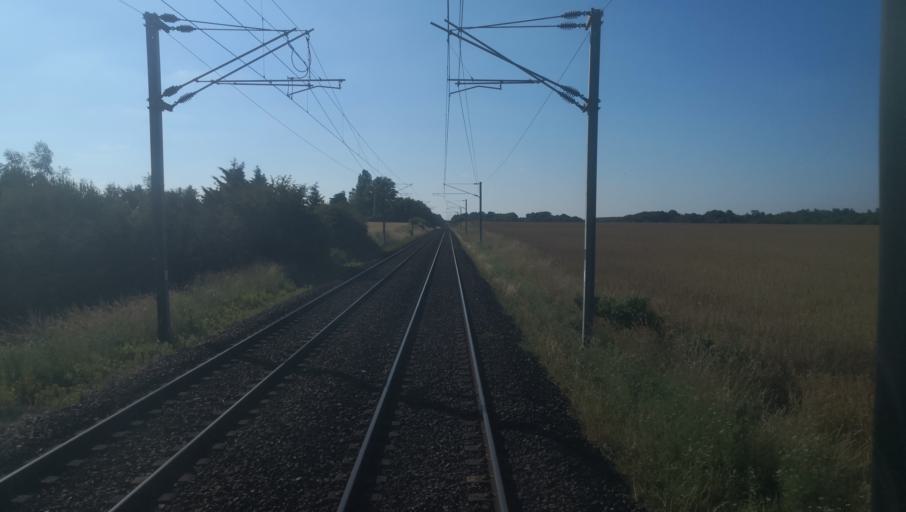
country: FR
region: Centre
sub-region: Departement du Loiret
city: Bonny-sur-Loire
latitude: 47.5874
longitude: 2.8096
